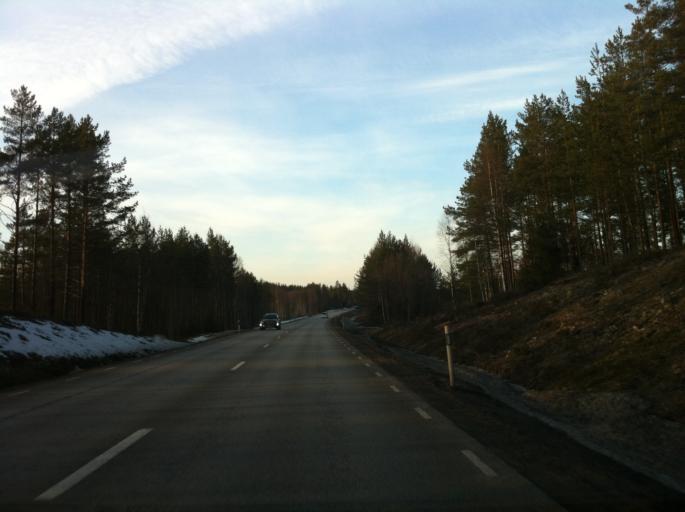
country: SE
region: Vaermland
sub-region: Filipstads Kommun
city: Lesjofors
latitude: 60.0432
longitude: 14.1453
